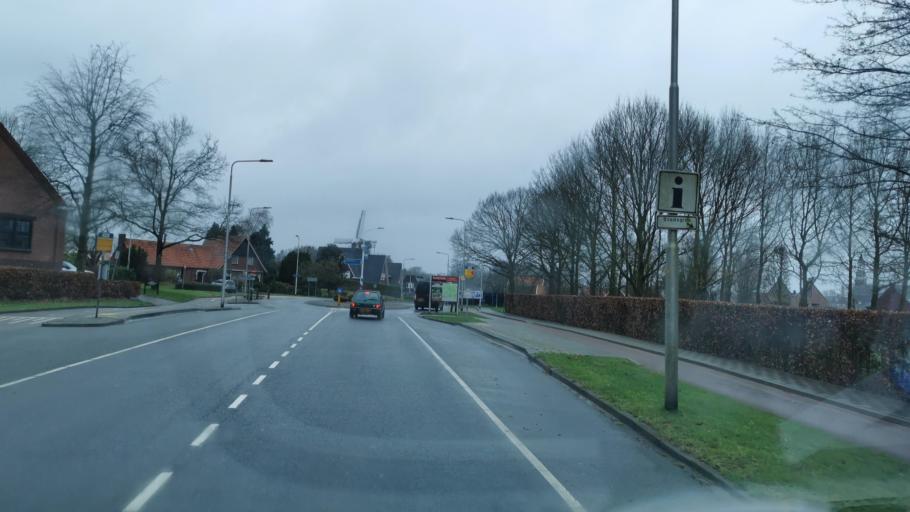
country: DE
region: Lower Saxony
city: Getelo
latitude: 52.4033
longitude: 6.8973
